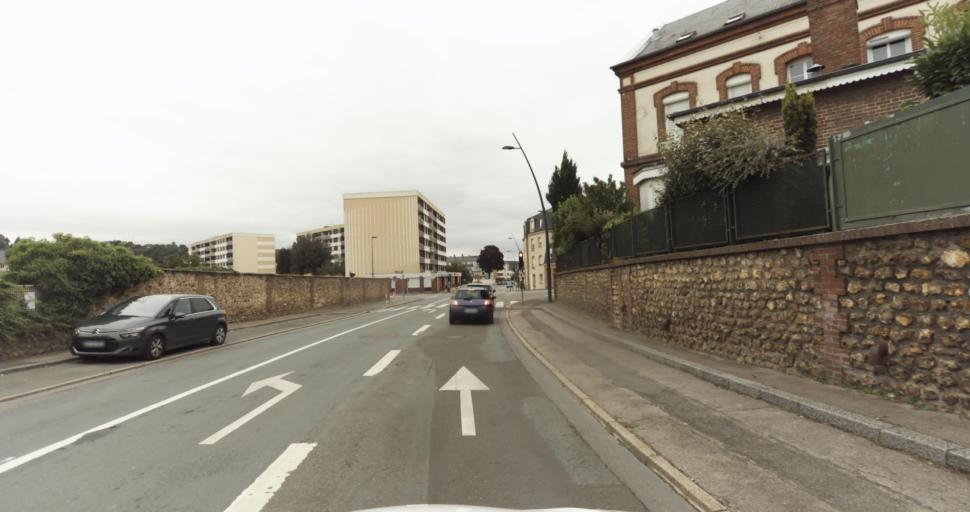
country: FR
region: Haute-Normandie
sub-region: Departement de l'Eure
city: Evreux
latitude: 49.0268
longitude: 1.1556
